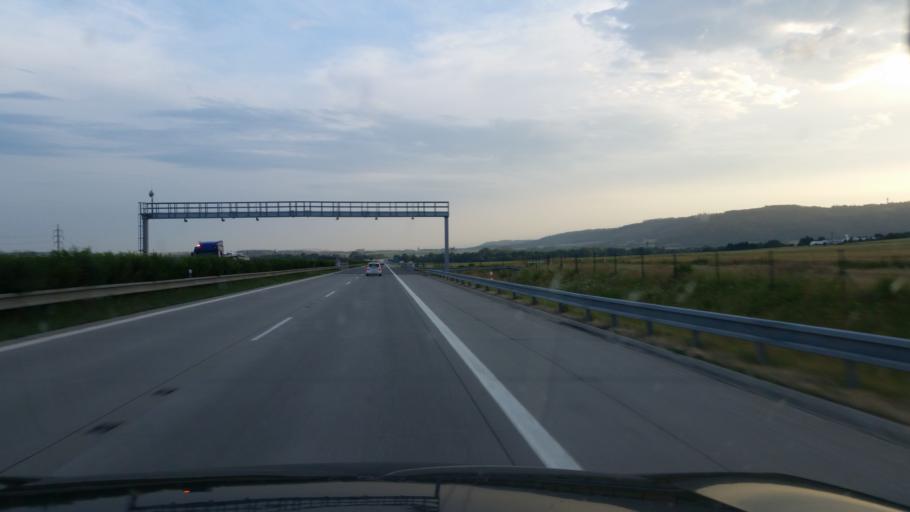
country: CZ
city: Jesenik nad Odrou
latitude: 49.6476
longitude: 17.8806
